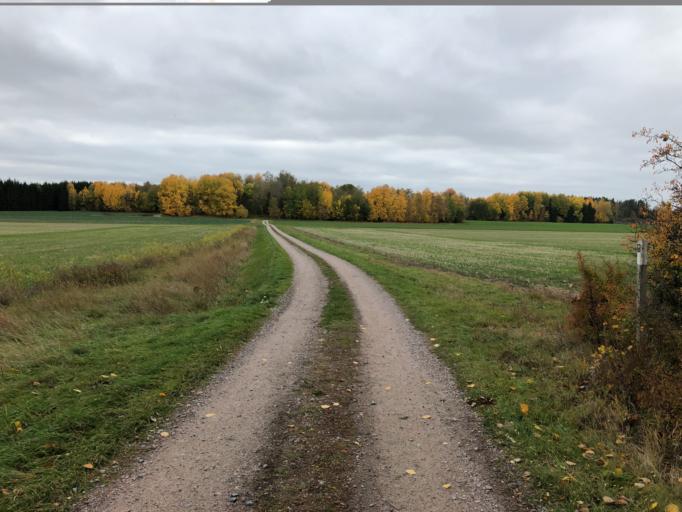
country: SE
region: Soedermanland
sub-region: Oxelosunds Kommun
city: Bara
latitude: 58.7188
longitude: 17.0477
